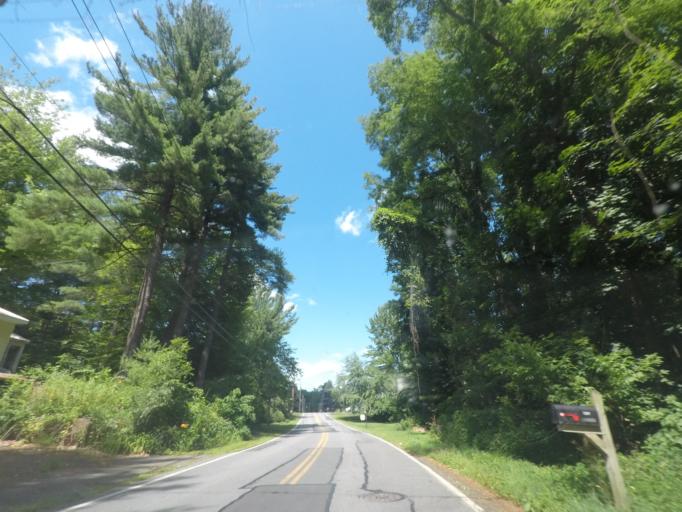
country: US
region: New York
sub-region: Schenectady County
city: Rotterdam
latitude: 42.7431
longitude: -73.9453
